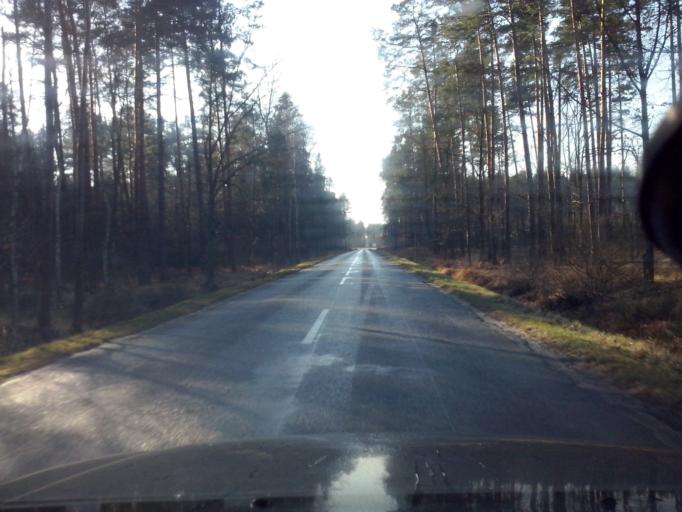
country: PL
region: Subcarpathian Voivodeship
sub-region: Powiat lezajski
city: Letownia
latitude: 50.3677
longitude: 22.2475
